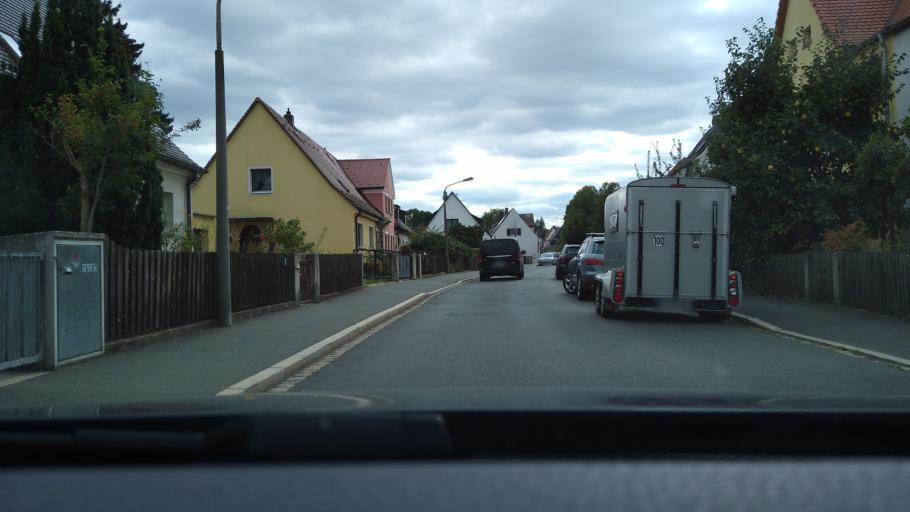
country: DE
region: Bavaria
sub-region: Regierungsbezirk Mittelfranken
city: Nuernberg
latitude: 49.4839
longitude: 11.1092
